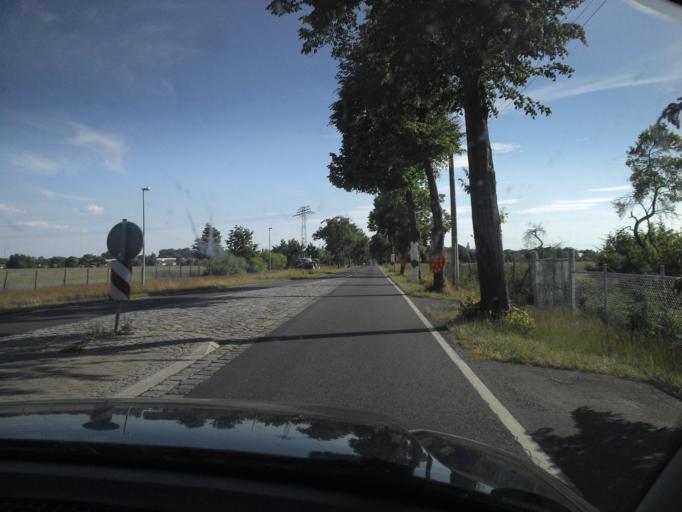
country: DE
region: Brandenburg
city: Vetschau
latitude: 51.7970
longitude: 14.0876
